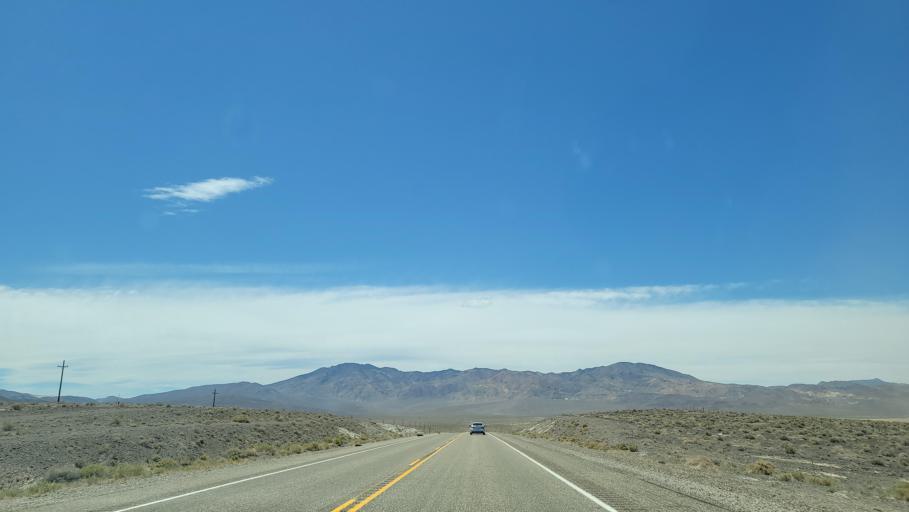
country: US
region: Nevada
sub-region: Mineral County
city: Hawthorne
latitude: 38.2452
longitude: -118.0548
